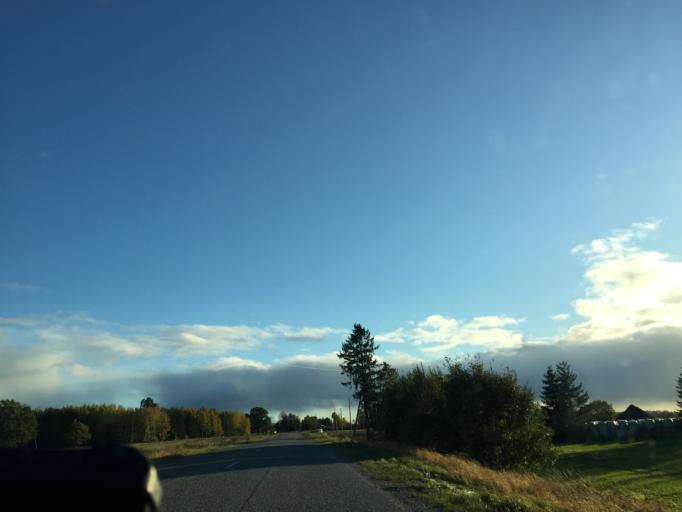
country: LV
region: Saldus Rajons
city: Saldus
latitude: 56.8404
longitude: 22.3792
